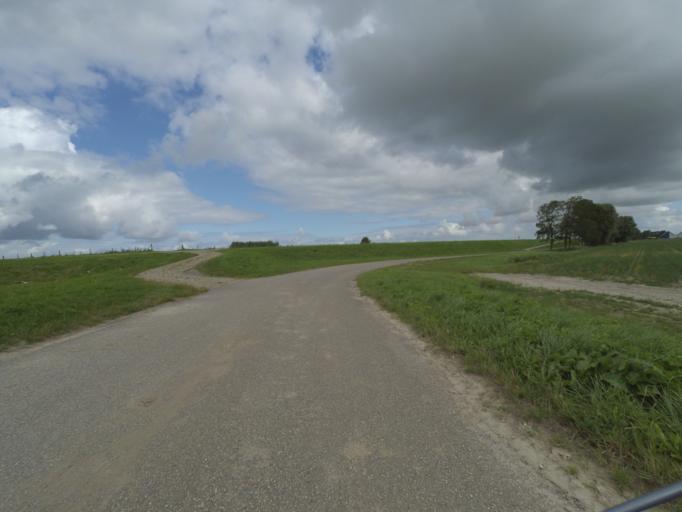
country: NL
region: Groningen
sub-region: Gemeente Zuidhorn
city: Grijpskerk
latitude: 53.3128
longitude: 6.2626
